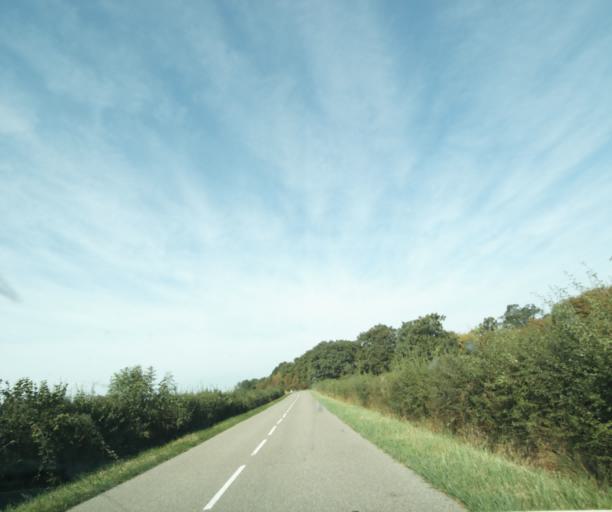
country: FR
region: Bourgogne
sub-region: Departement de Saone-et-Loire
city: Genelard
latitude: 46.5694
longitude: 4.2717
